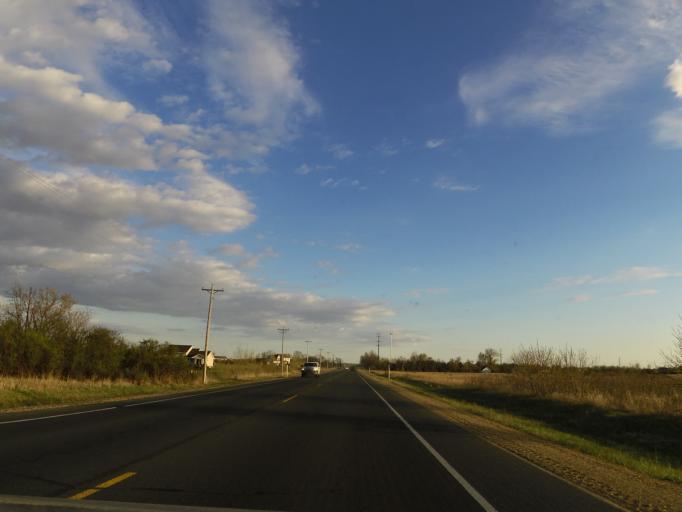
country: US
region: Wisconsin
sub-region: Saint Croix County
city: North Hudson
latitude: 45.0111
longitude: -92.6755
